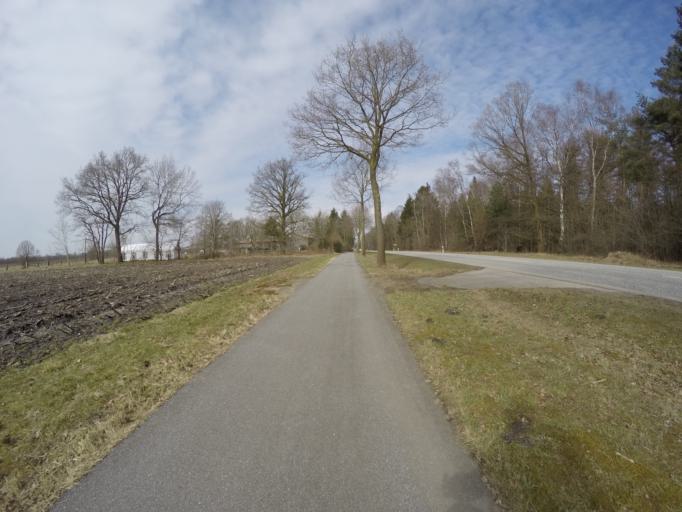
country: DE
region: Schleswig-Holstein
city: Heidmoor
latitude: 53.8263
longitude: 9.8828
